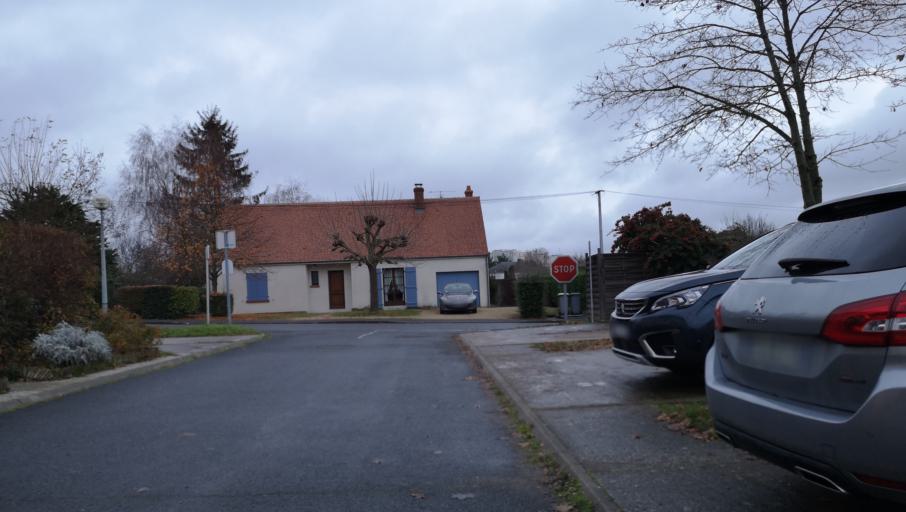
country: FR
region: Centre
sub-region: Departement du Loiret
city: Saint-Jean-de-Braye
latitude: 47.9064
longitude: 1.9634
